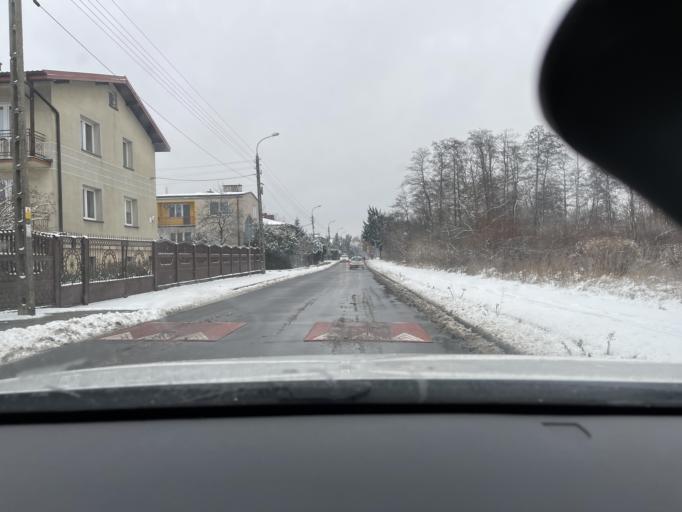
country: PL
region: Masovian Voivodeship
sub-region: Powiat zyrardowski
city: Zyrardow
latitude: 52.0435
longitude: 20.4452
